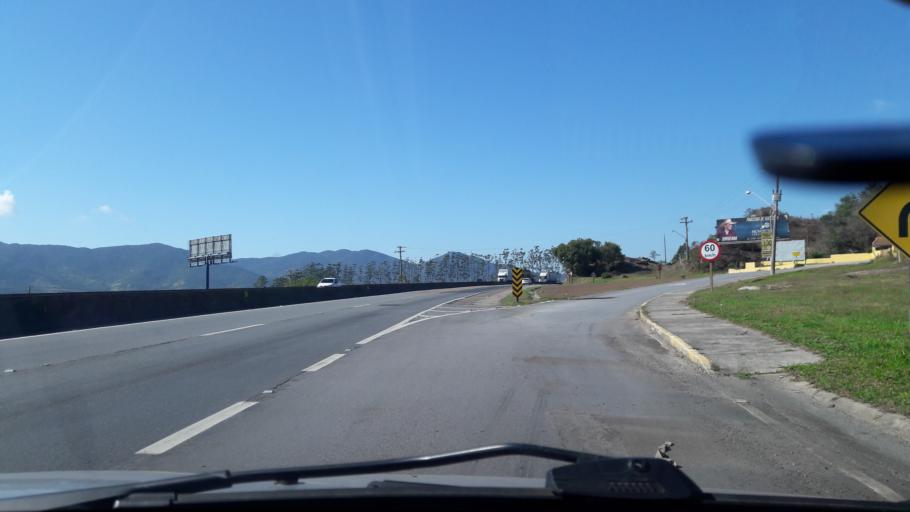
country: BR
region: Santa Catarina
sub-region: Tijucas
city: Tijucas
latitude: -27.3200
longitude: -48.6283
